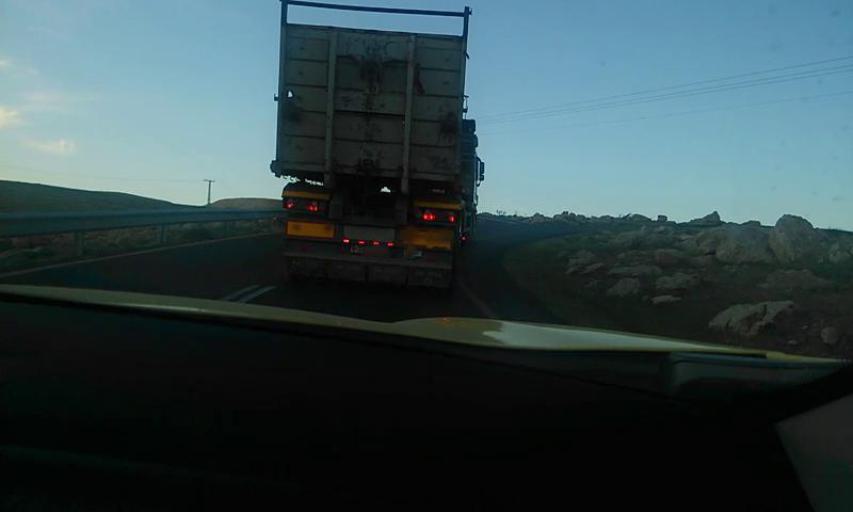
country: PS
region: West Bank
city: Rammun
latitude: 31.9168
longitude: 35.3479
